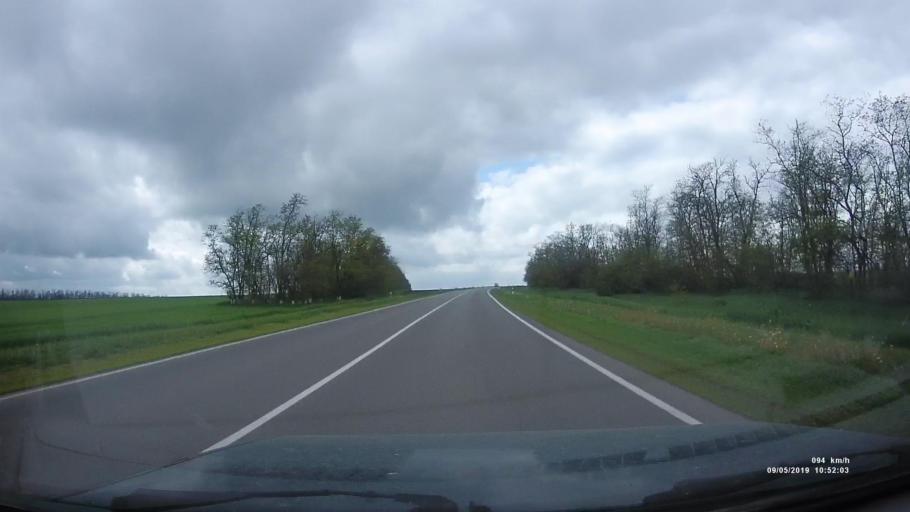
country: RU
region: Rostov
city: Peshkovo
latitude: 46.9060
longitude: 39.3549
